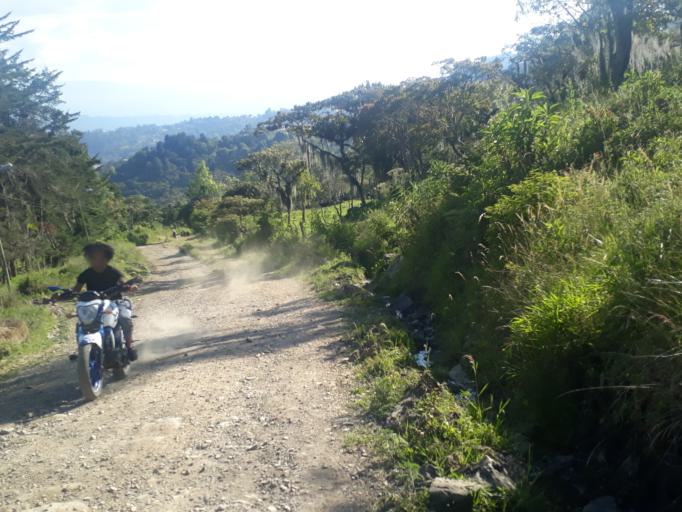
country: CO
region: Santander
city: Velez
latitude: 6.0276
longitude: -73.6669
